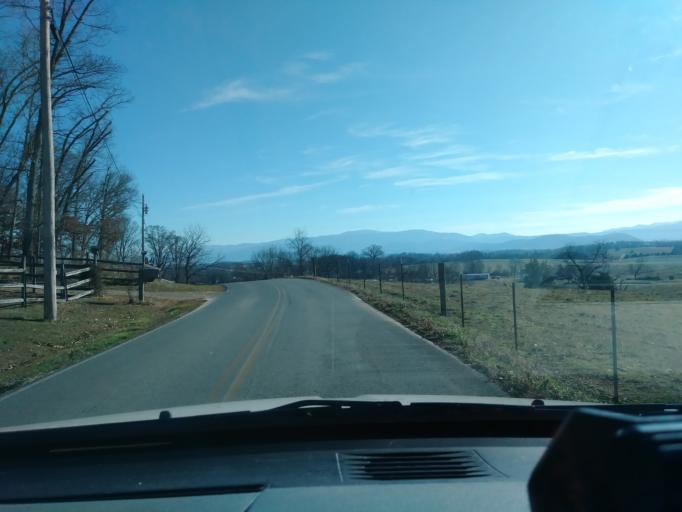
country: US
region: Tennessee
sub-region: Greene County
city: Greeneville
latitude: 36.0897
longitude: -82.9046
